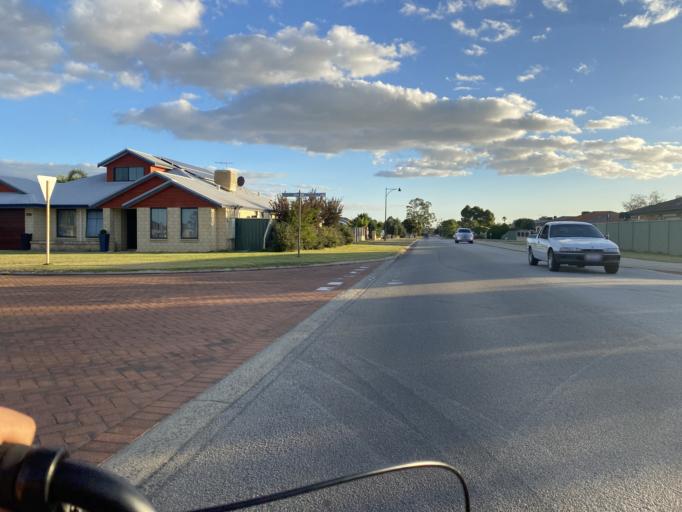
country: AU
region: Western Australia
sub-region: Kalamunda
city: Maida Vale
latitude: -31.9699
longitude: 116.0063
